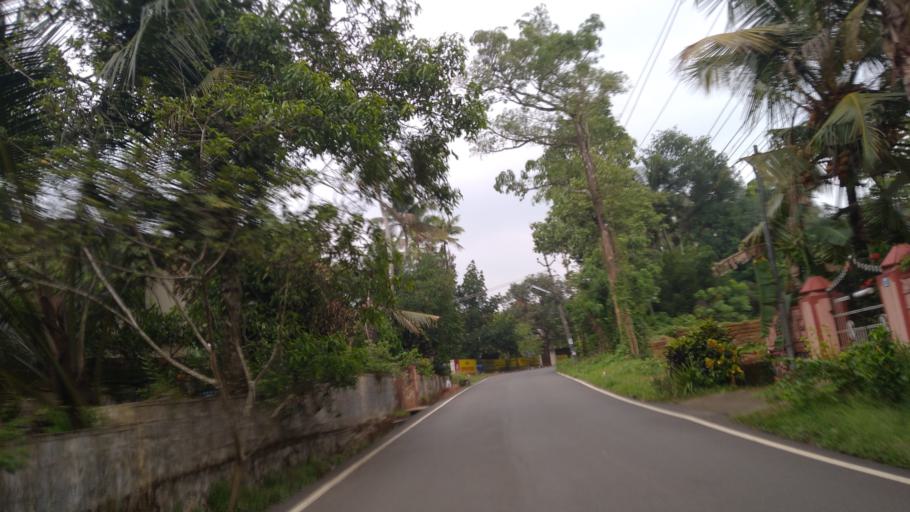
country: IN
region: Kerala
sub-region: Ernakulam
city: Perumbavoor
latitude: 10.0555
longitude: 76.5058
